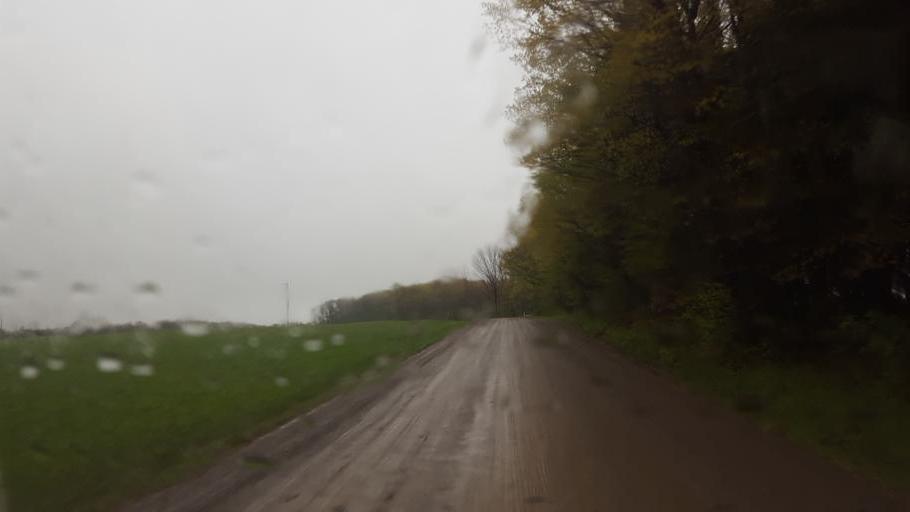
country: US
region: Pennsylvania
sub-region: Tioga County
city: Westfield
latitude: 42.0586
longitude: -77.4665
